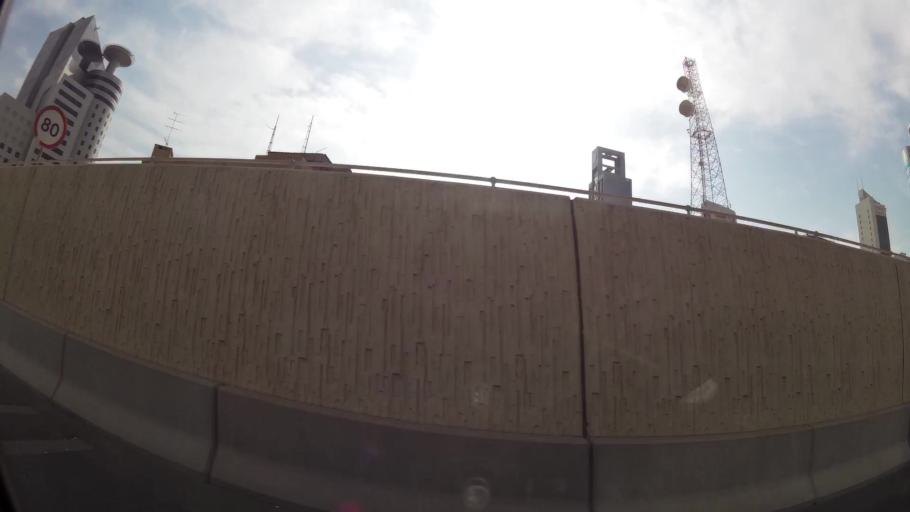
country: KW
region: Al Asimah
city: Kuwait City
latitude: 29.3658
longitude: 47.9620
